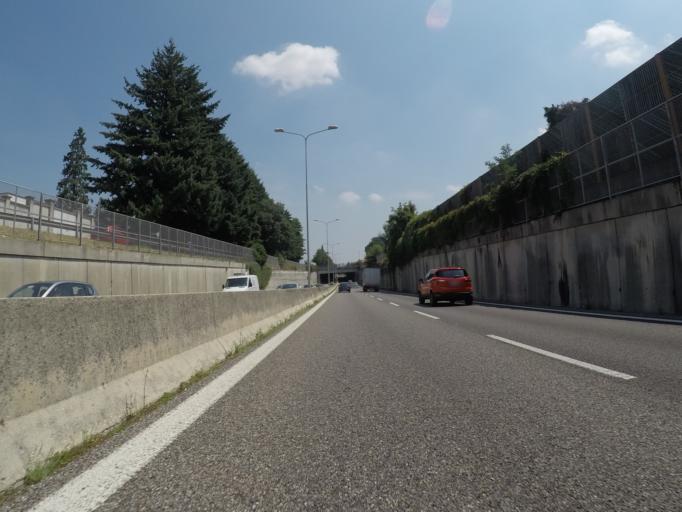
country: IT
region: Lombardy
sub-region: Provincia di Varese
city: Cardano al Campo
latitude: 45.6435
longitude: 8.7654
